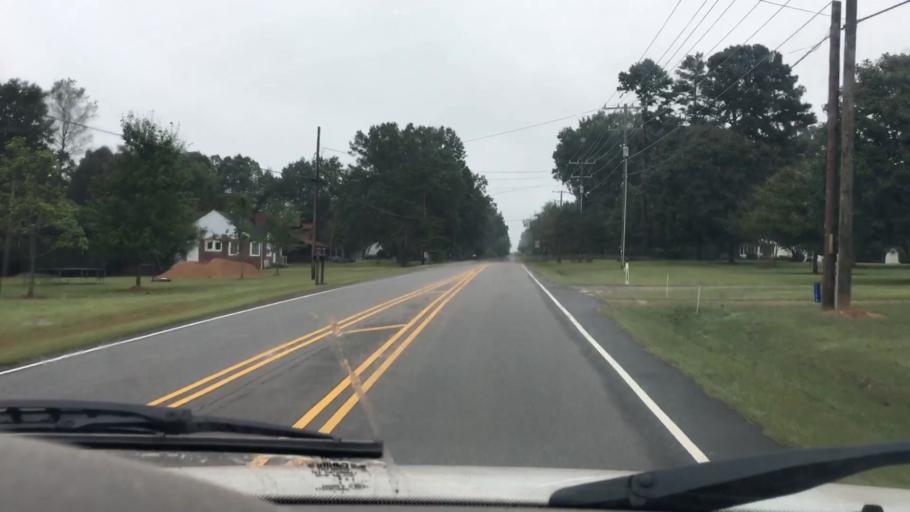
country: US
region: North Carolina
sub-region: Iredell County
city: Mooresville
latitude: 35.6211
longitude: -80.7833
